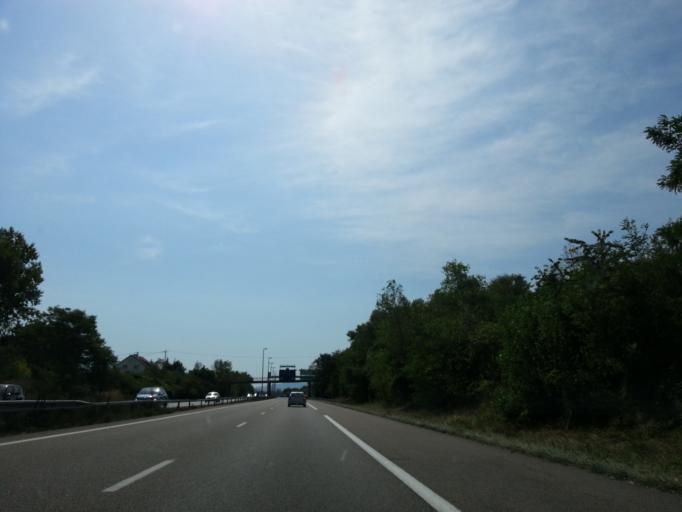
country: FR
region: Alsace
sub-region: Departement du Haut-Rhin
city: Blotzheim
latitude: 47.6086
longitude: 7.5252
